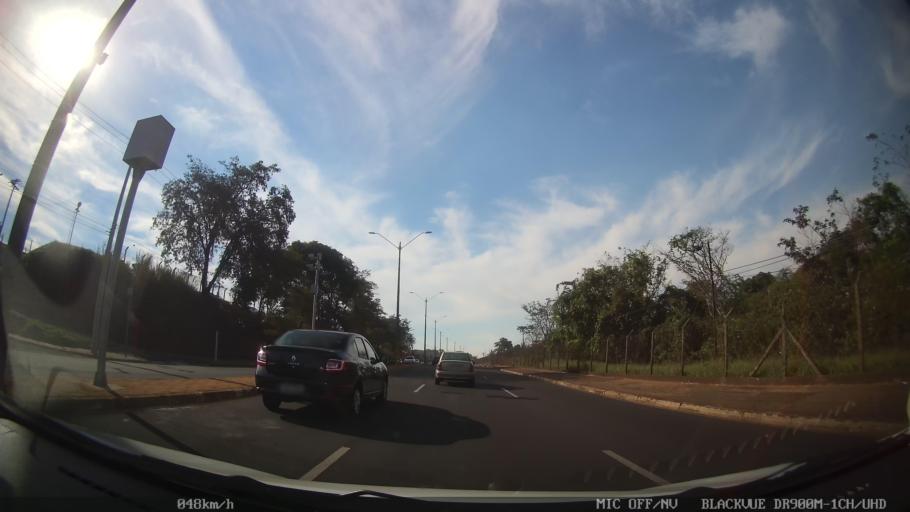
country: BR
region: Sao Paulo
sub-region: Araraquara
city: Araraquara
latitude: -21.7732
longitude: -48.1663
